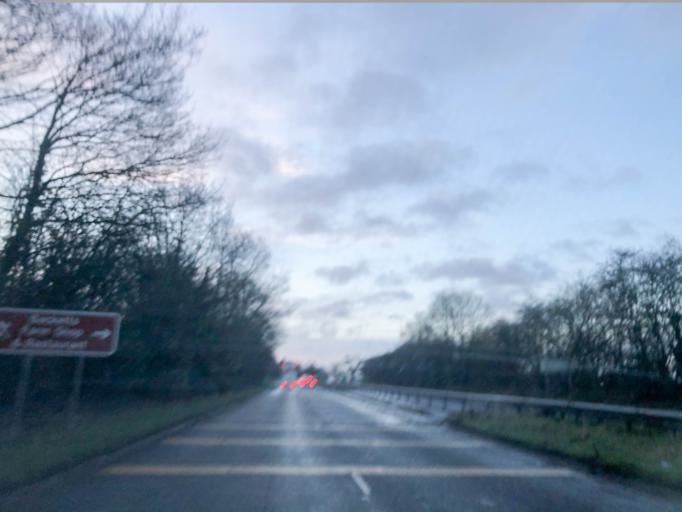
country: GB
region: England
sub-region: Solihull
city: Tidbury Green
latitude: 52.3762
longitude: -1.8870
